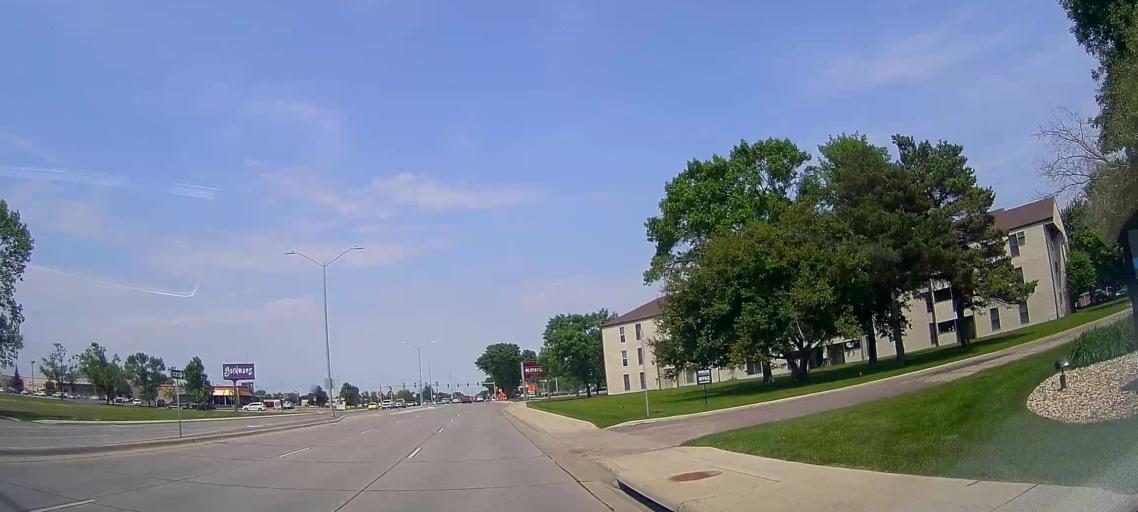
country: US
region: South Dakota
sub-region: Minnehaha County
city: Sioux Falls
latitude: 43.5085
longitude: -96.7710
